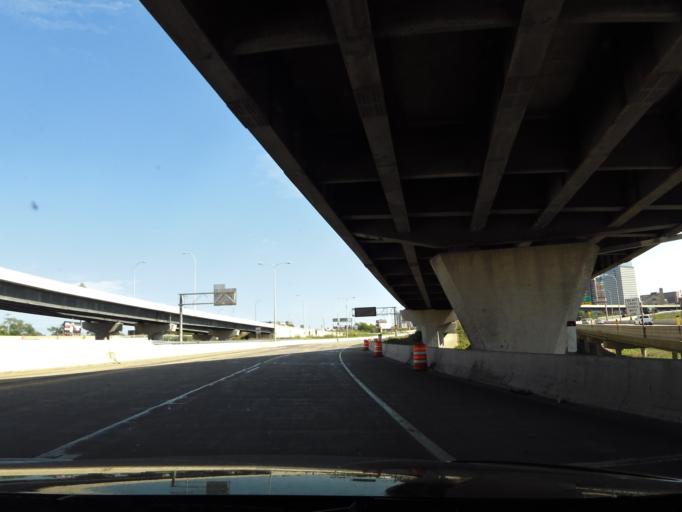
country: US
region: Minnesota
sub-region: Hennepin County
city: Minneapolis
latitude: 44.9742
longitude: -93.2921
